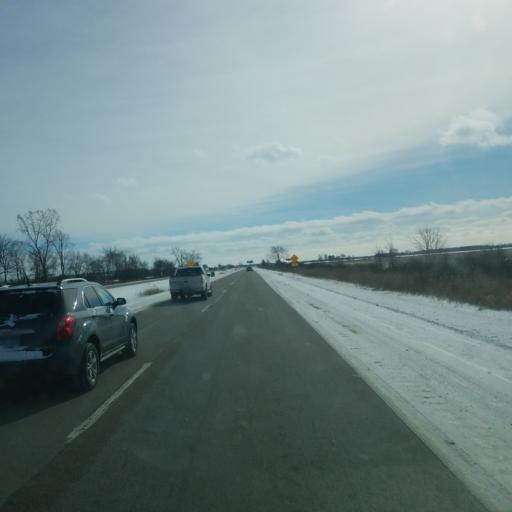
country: US
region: Michigan
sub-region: Gratiot County
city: Ithaca
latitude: 43.2766
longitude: -84.5718
